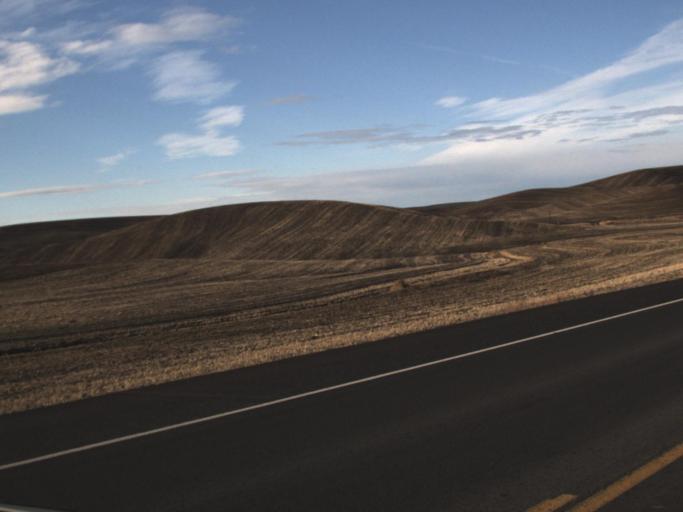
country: US
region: Washington
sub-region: Whitman County
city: Pullman
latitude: 46.7344
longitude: -117.2178
